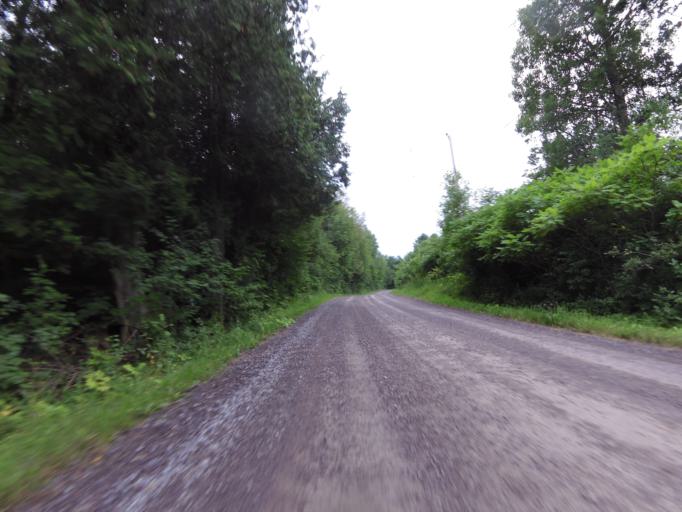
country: CA
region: Ontario
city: Carleton Place
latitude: 45.1502
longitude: -76.2132
